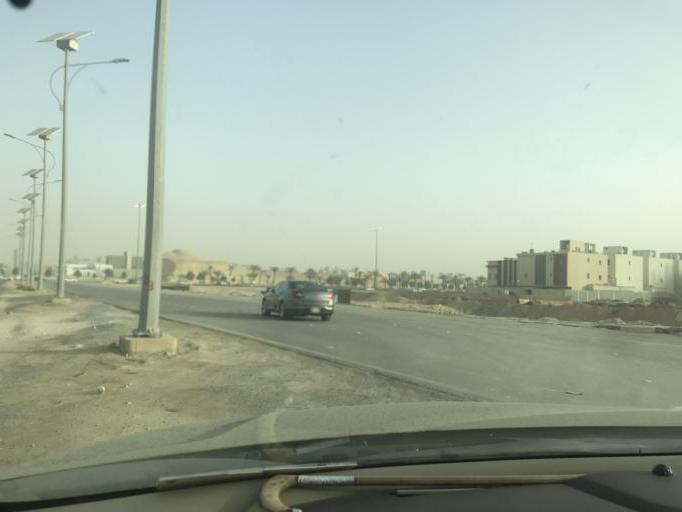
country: SA
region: Ar Riyad
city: Riyadh
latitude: 24.8455
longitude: 46.6643
